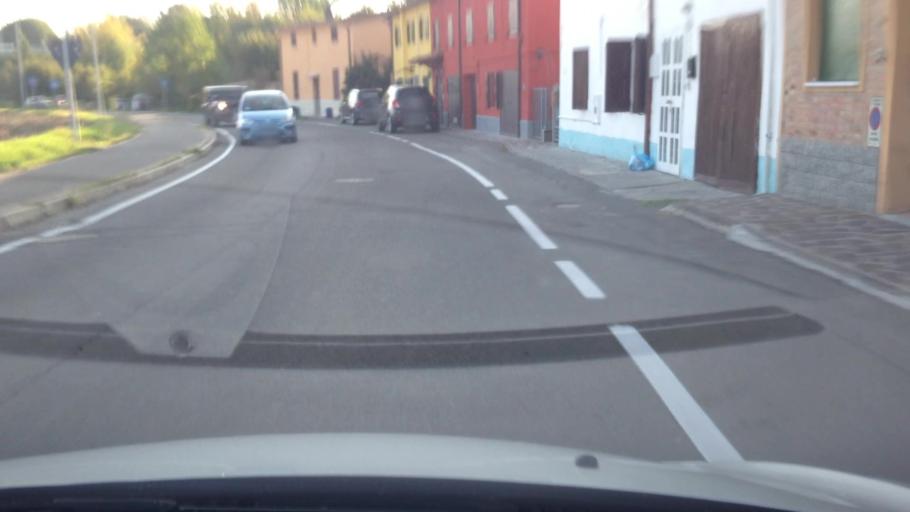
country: IT
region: Emilia-Romagna
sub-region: Provincia di Modena
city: Baggiovara
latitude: 44.6190
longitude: 10.8892
